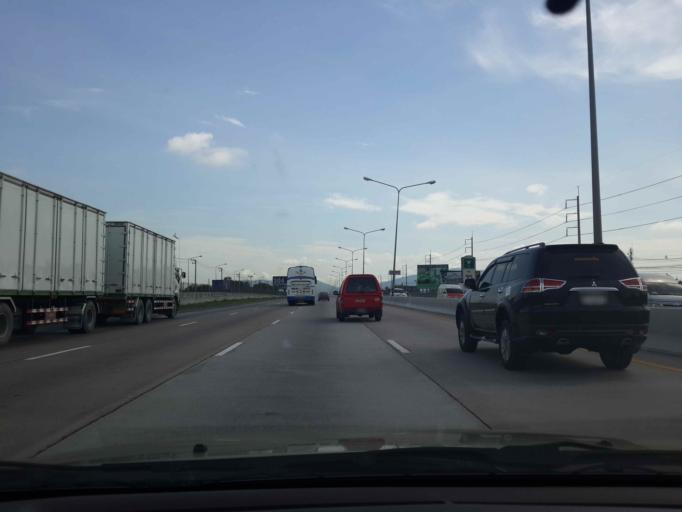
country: TH
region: Chon Buri
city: Si Racha
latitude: 13.1602
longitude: 100.9887
